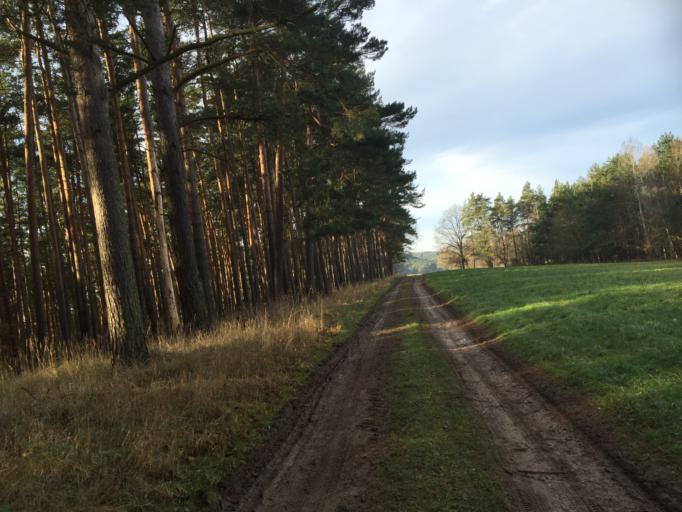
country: DE
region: Thuringia
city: Orlamunde
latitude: 50.7847
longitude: 11.5253
